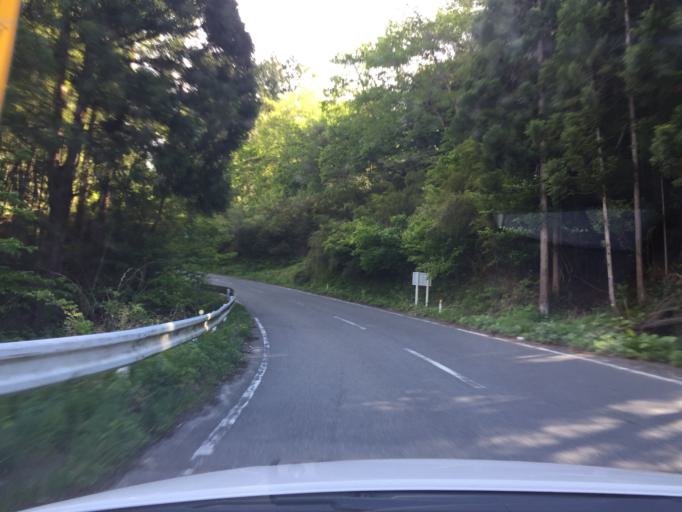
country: JP
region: Miyagi
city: Marumori
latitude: 37.7369
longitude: 140.8030
